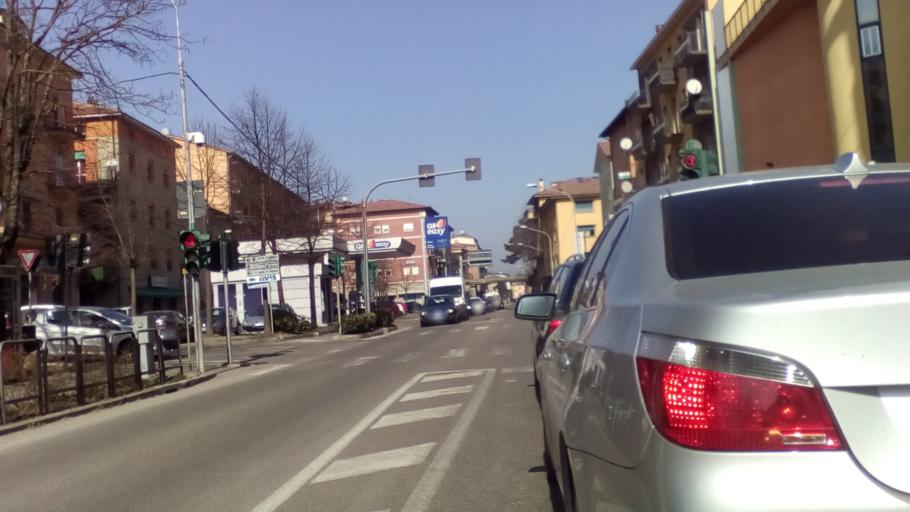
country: IT
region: Emilia-Romagna
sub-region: Provincia di Modena
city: Pavullo nel Frignano
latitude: 44.3350
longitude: 10.8327
